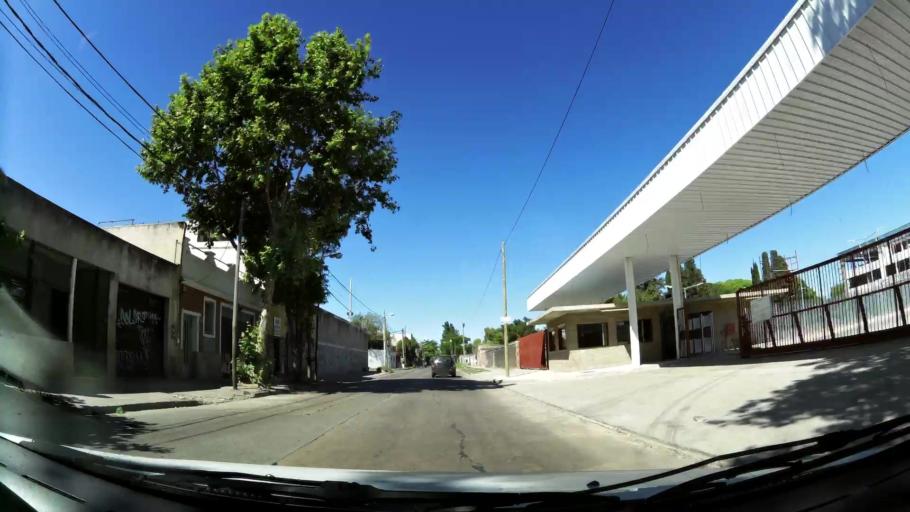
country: AR
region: Buenos Aires
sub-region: Partido de General San Martin
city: General San Martin
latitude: -34.5626
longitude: -58.5291
